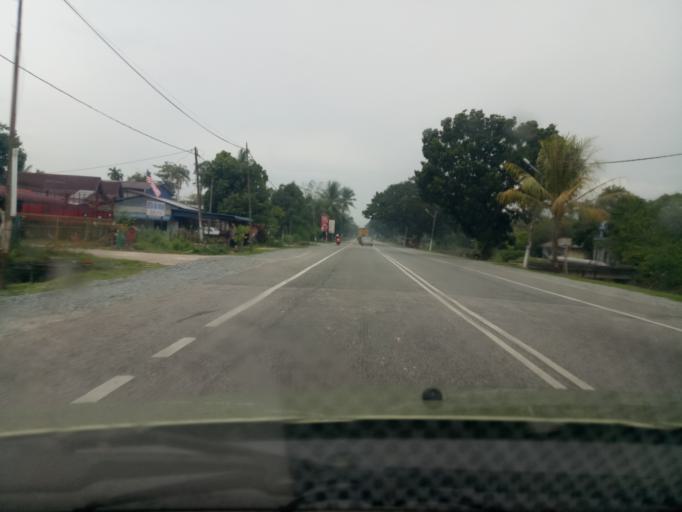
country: MY
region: Kedah
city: Gurun
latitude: 5.8861
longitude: 100.4440
